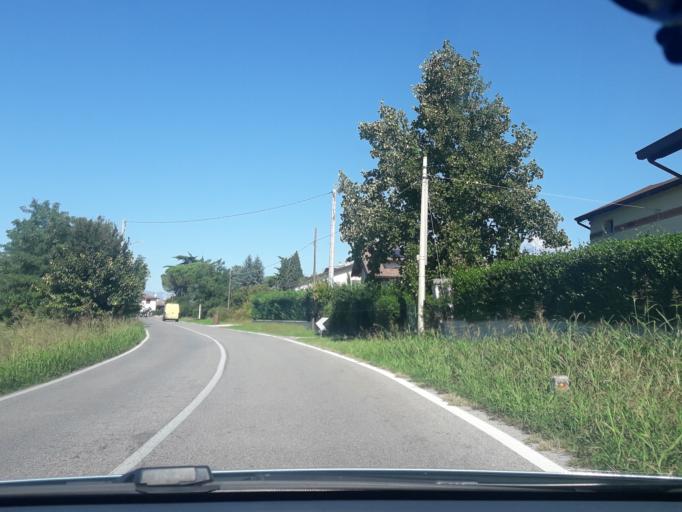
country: IT
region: Friuli Venezia Giulia
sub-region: Provincia di Udine
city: Basaldella
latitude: 46.0347
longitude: 13.2357
